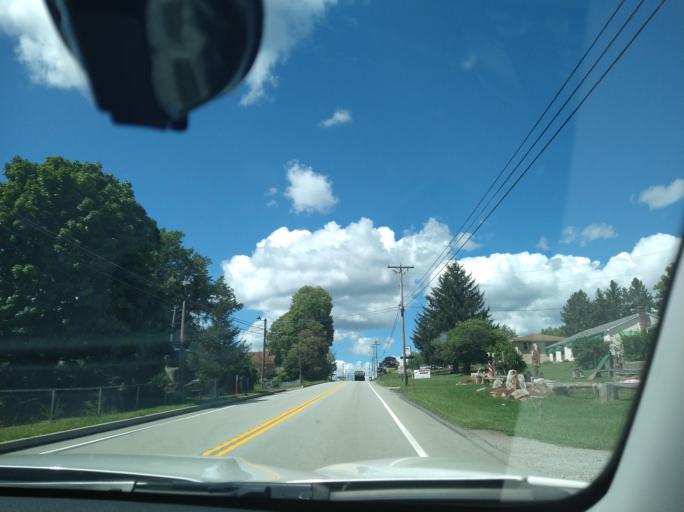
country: US
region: Pennsylvania
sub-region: Fayette County
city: Bear Rocks
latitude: 40.0968
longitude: -79.3559
